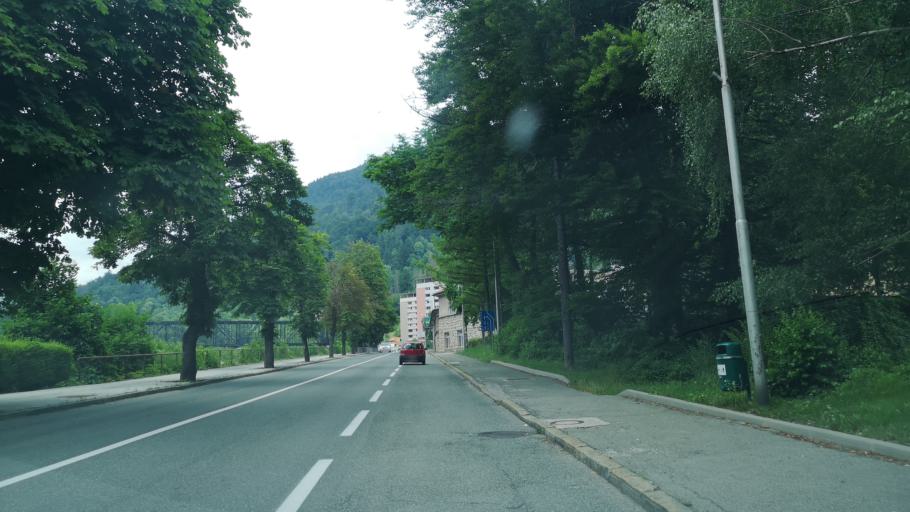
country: SI
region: Jesenice
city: Jesenice
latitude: 46.4338
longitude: 14.0613
